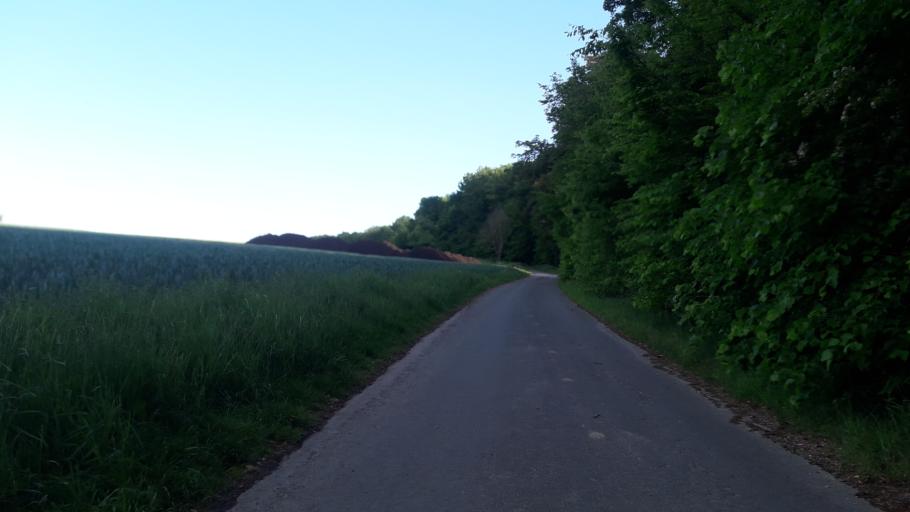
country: DE
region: North Rhine-Westphalia
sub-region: Regierungsbezirk Detmold
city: Paderborn
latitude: 51.6696
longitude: 8.7854
